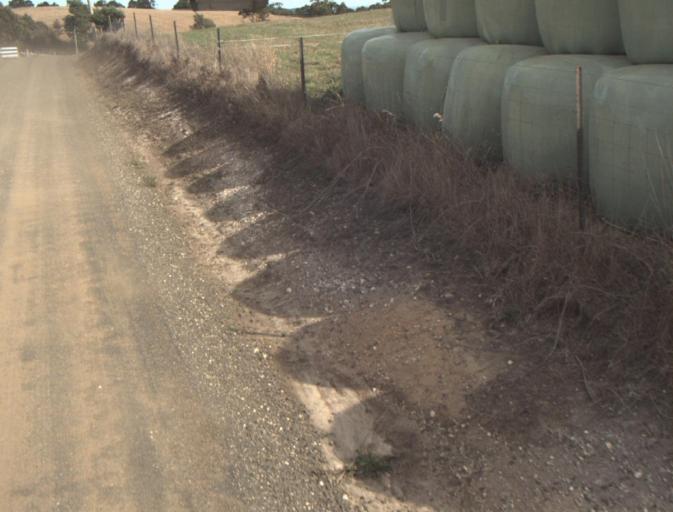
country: AU
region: Tasmania
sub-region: Launceston
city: Mayfield
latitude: -41.1894
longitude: 147.1906
